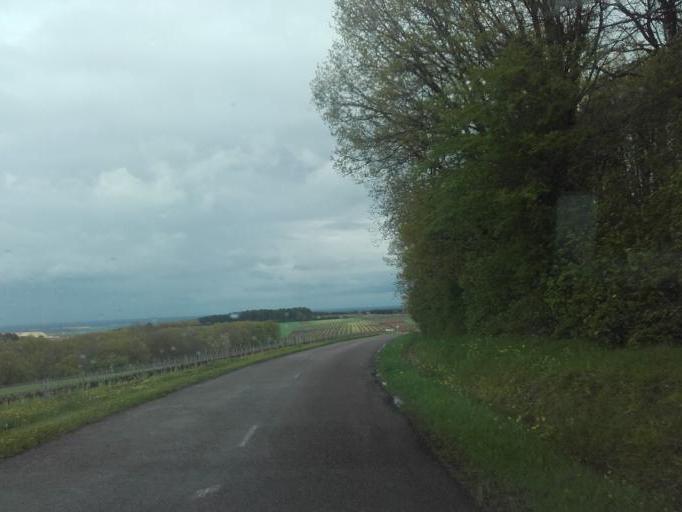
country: FR
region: Bourgogne
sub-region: Departement de la Cote-d'Or
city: Nuits-Saint-Georges
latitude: 47.1042
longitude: 4.8847
